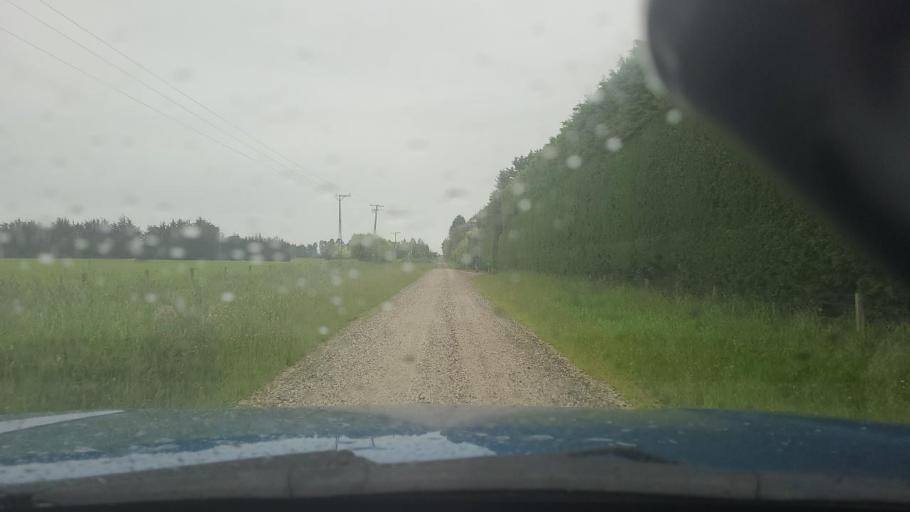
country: NZ
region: Southland
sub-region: Invercargill City
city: Invercargill
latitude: -46.3708
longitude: 168.5700
